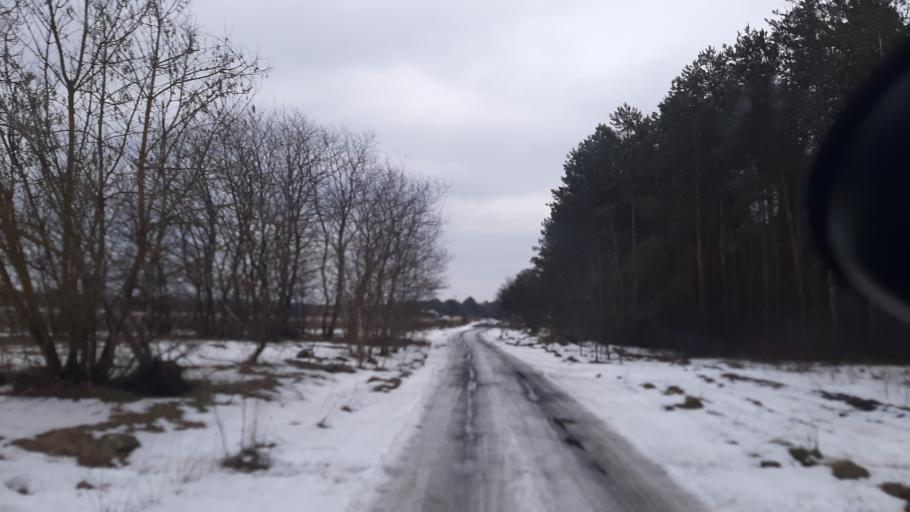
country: PL
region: Lublin Voivodeship
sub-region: Powiat wlodawski
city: Wlodawa
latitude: 51.5174
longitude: 23.5951
